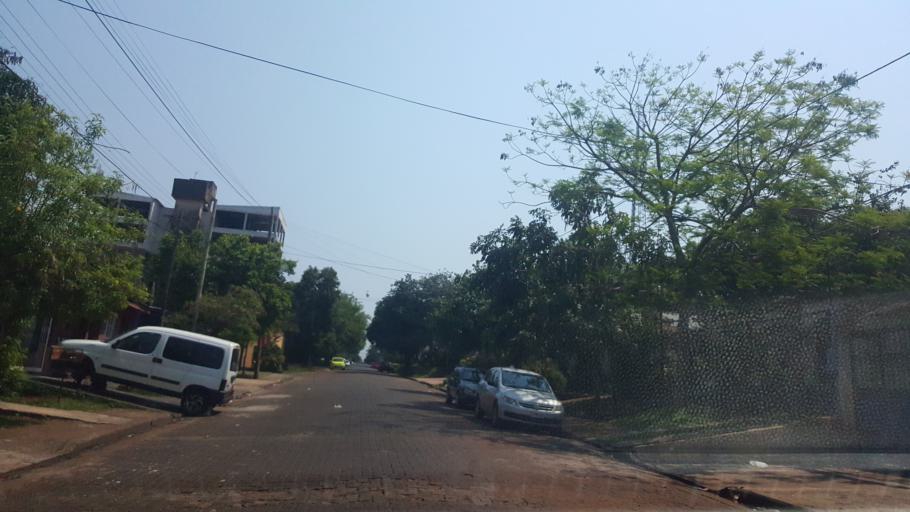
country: AR
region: Misiones
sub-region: Departamento de Capital
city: Posadas
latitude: -27.4015
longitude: -55.9066
